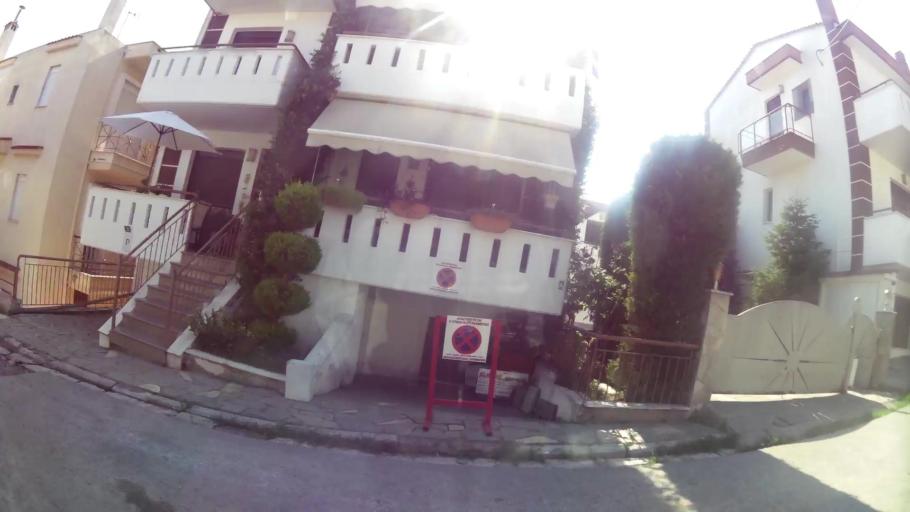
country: GR
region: Central Macedonia
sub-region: Nomos Thessalonikis
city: Neo Rysi
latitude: 40.4949
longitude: 22.9907
